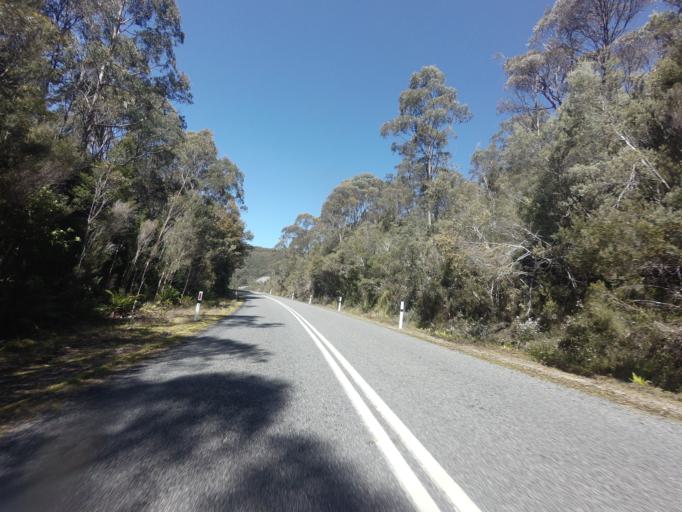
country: AU
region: Tasmania
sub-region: Huon Valley
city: Geeveston
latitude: -42.8143
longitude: 146.3803
